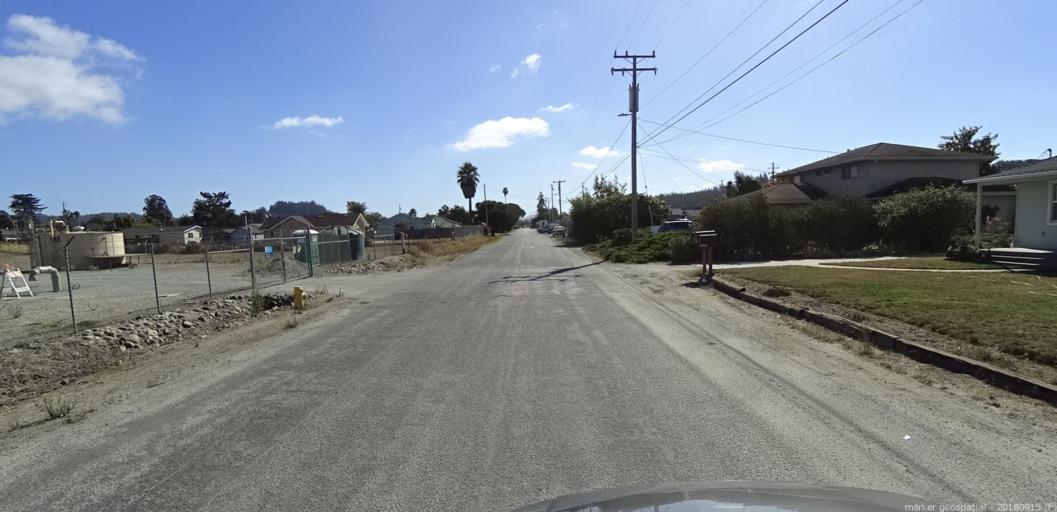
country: US
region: California
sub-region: Monterey County
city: Las Lomas
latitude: 36.8633
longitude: -121.7380
